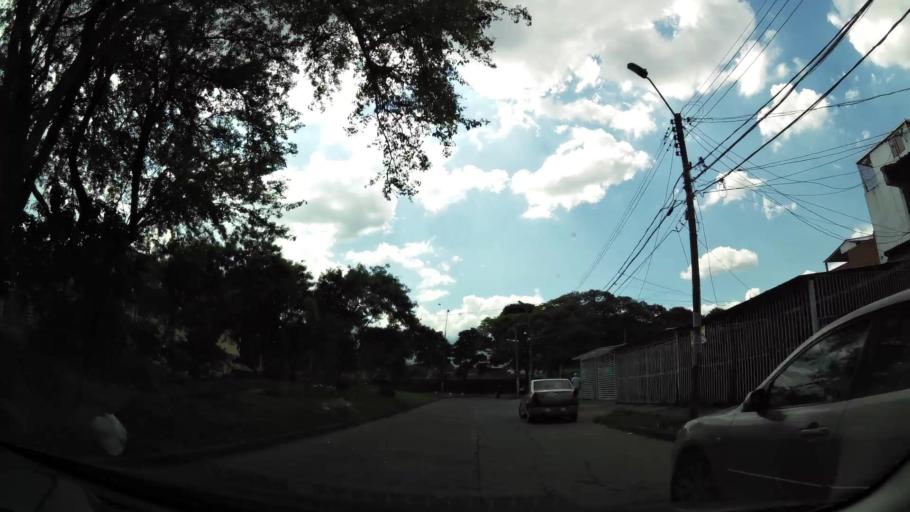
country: CO
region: Valle del Cauca
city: Cali
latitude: 3.4099
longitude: -76.5210
